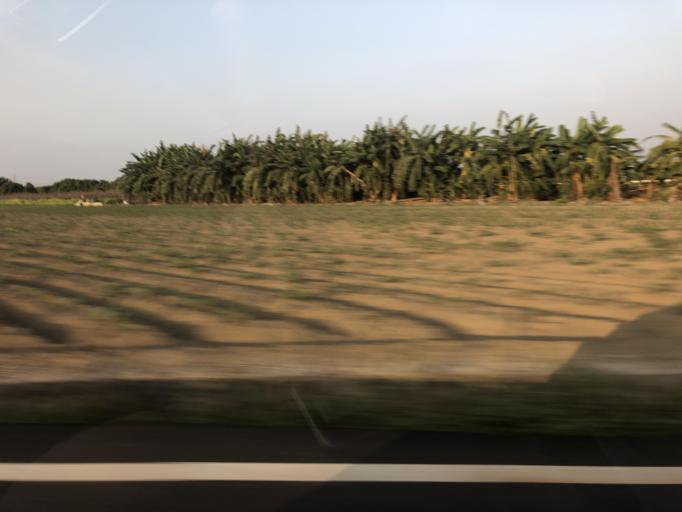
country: TW
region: Taiwan
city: Xinying
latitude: 23.1577
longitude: 120.2739
